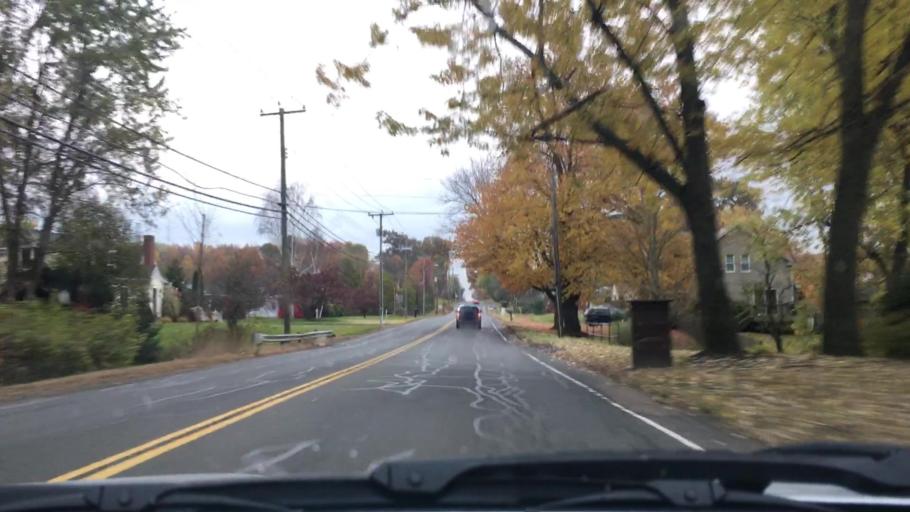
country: US
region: Massachusetts
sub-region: Hampden County
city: Agawam
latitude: 42.0658
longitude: -72.6924
